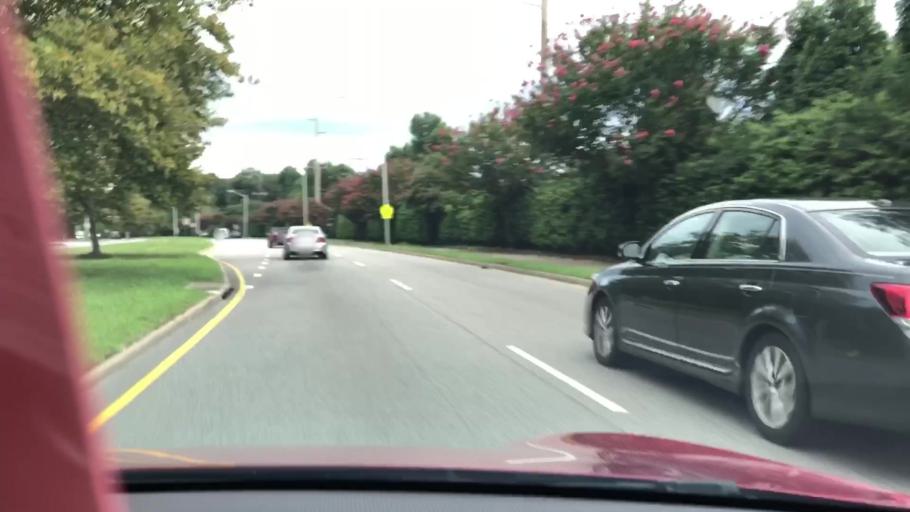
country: US
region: Virginia
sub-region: City of Virginia Beach
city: Virginia Beach
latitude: 36.8882
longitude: -76.0502
